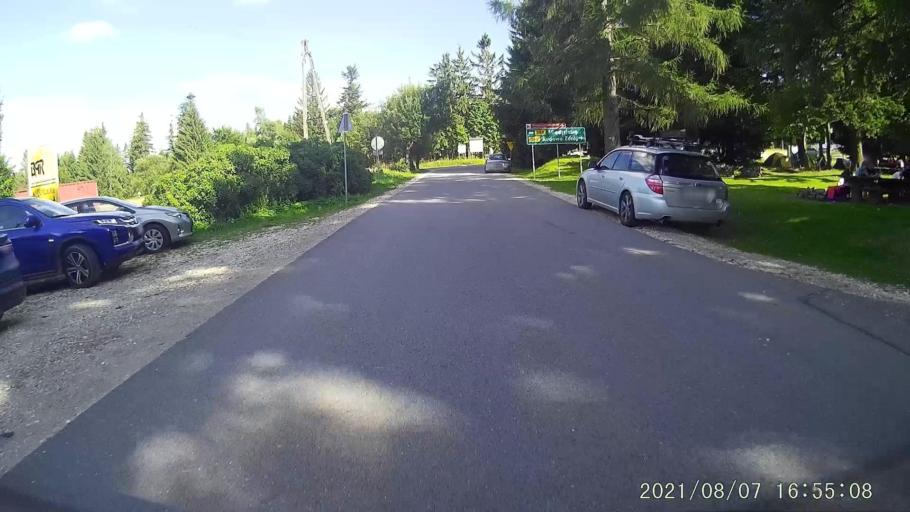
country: PL
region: Lower Silesian Voivodeship
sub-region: Powiat klodzki
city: Bystrzyca Klodzka
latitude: 50.2773
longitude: 16.5379
